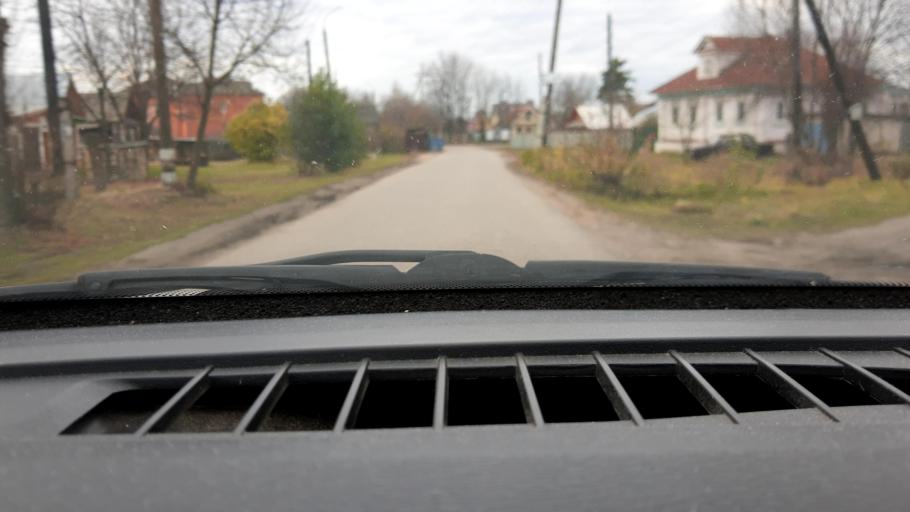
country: RU
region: Nizjnij Novgorod
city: Gorodets
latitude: 56.6419
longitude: 43.4710
